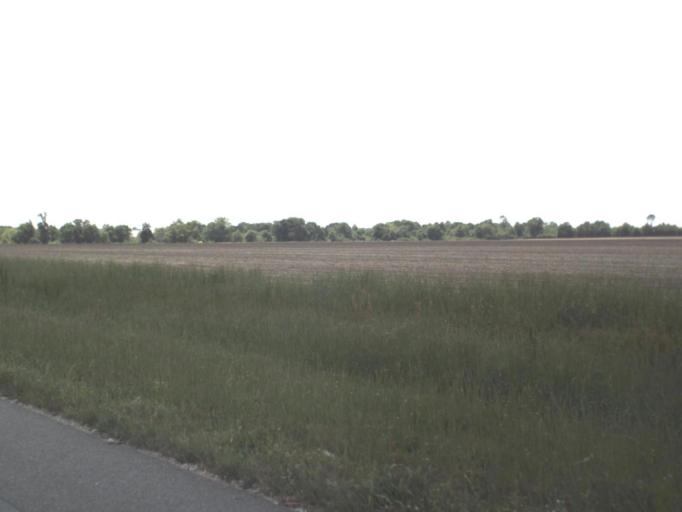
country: US
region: Alabama
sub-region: Escambia County
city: Atmore
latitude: 30.9938
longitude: -87.4896
